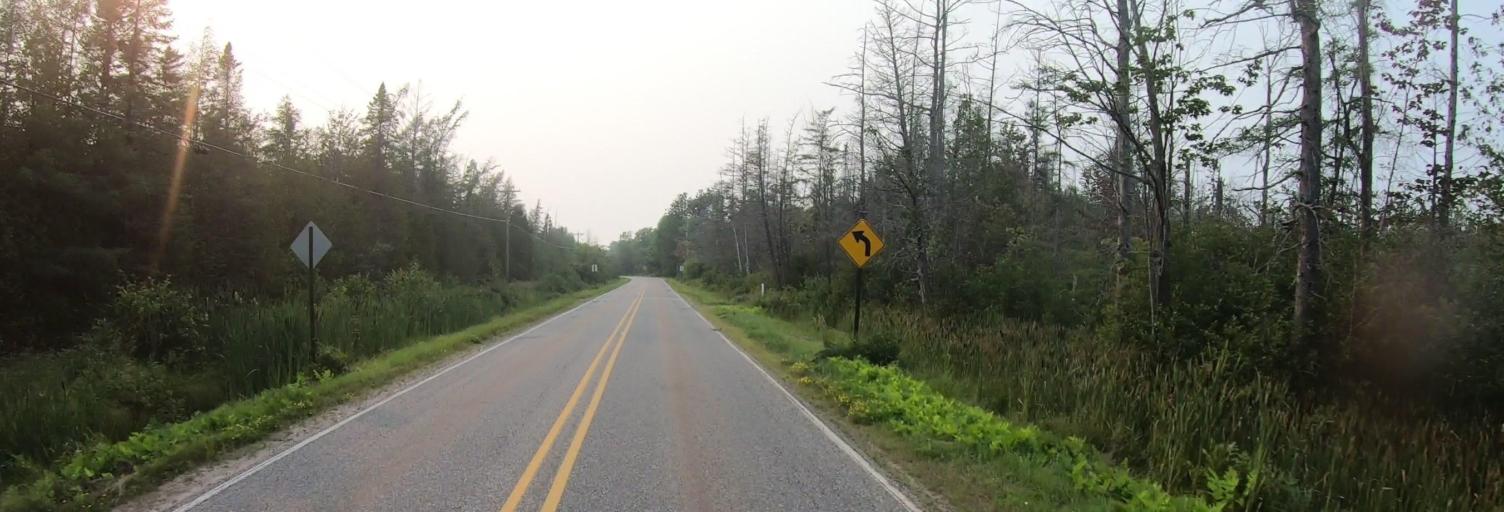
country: US
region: Michigan
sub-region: Chippewa County
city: Sault Ste. Marie
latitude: 46.4840
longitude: -84.6672
